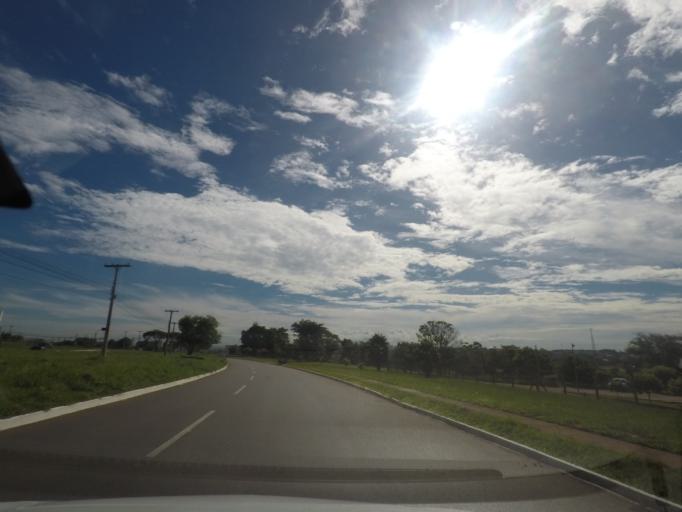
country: BR
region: Goias
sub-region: Aparecida De Goiania
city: Aparecida de Goiania
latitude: -16.8002
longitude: -49.2570
